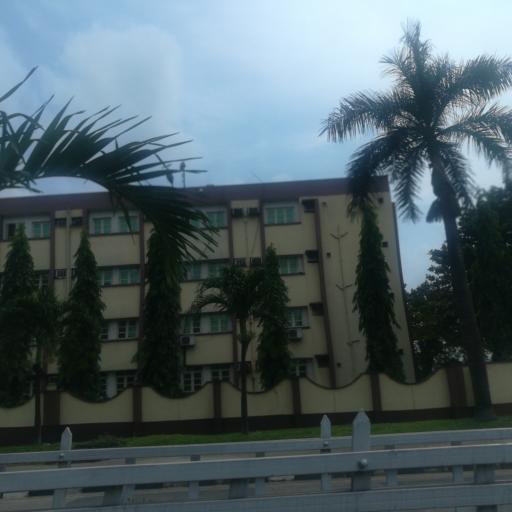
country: NG
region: Lagos
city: Ikeja
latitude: 6.6134
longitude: 3.3600
